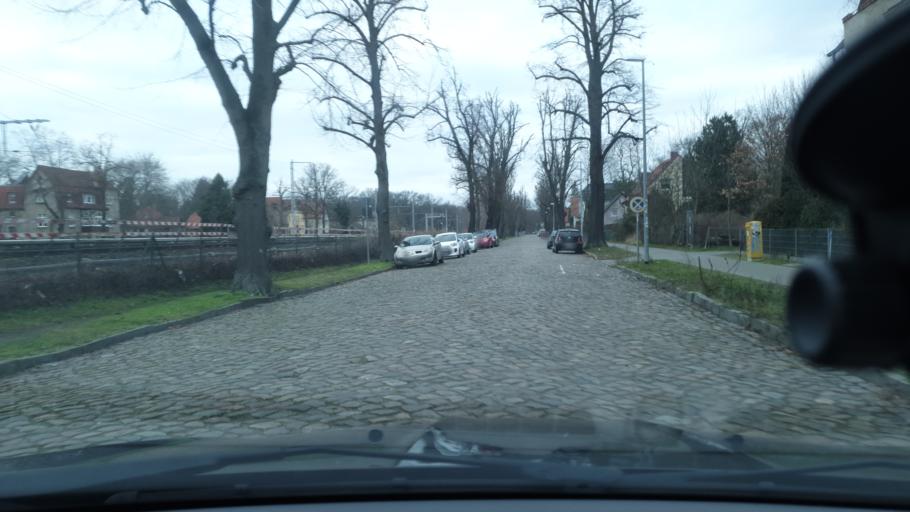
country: DE
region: Brandenburg
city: Zeuthen
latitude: 52.3728
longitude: 13.6147
